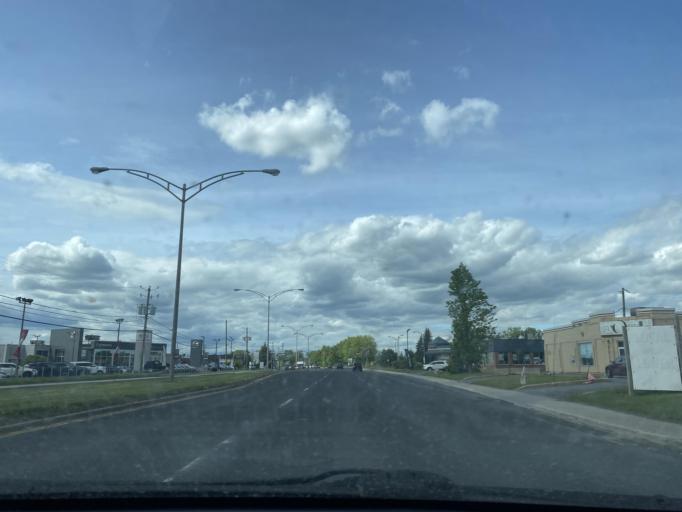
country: CA
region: Quebec
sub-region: Monteregie
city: Carignan
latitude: 45.4547
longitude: -73.3019
